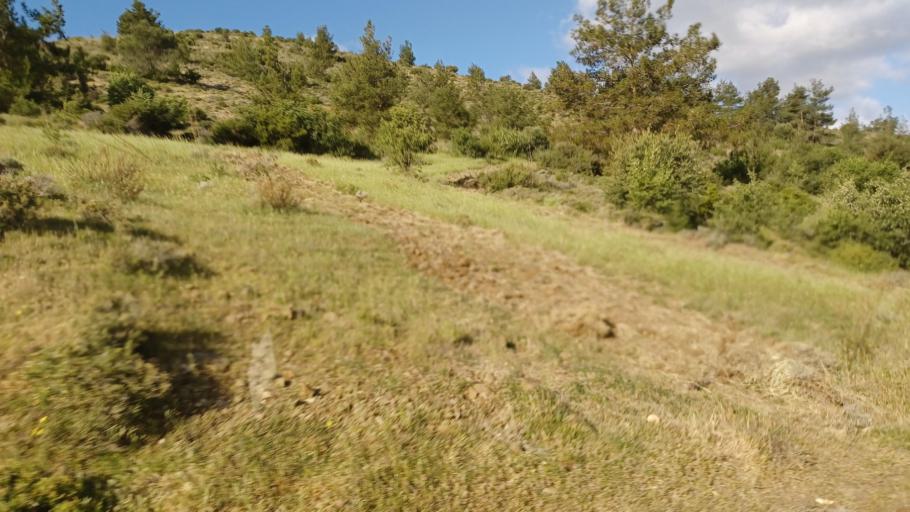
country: CY
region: Lefkosia
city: Peristerona
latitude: 35.0656
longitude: 33.0492
